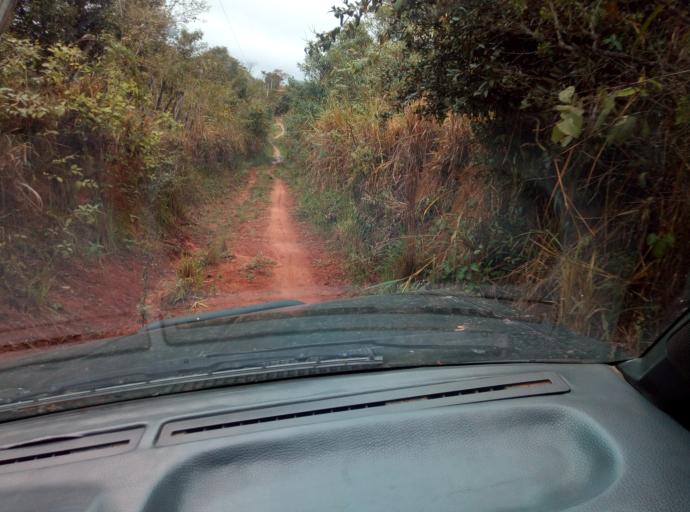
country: PY
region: Caaguazu
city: Carayao
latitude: -25.1960
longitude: -56.3544
